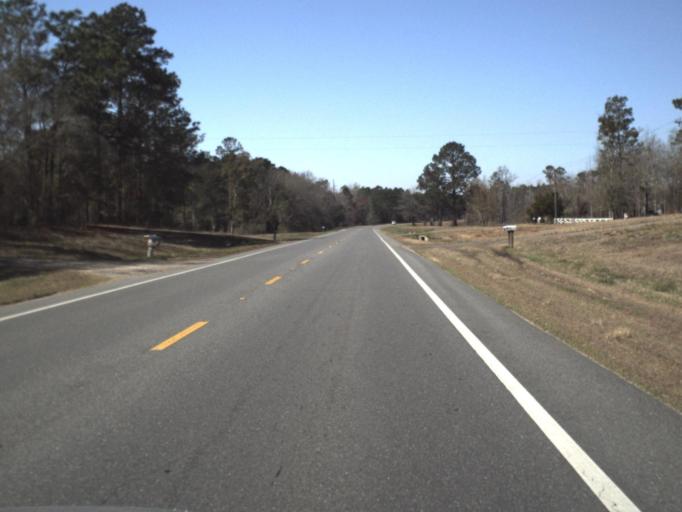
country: US
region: Florida
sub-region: Jackson County
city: Sneads
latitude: 30.7198
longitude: -85.0656
